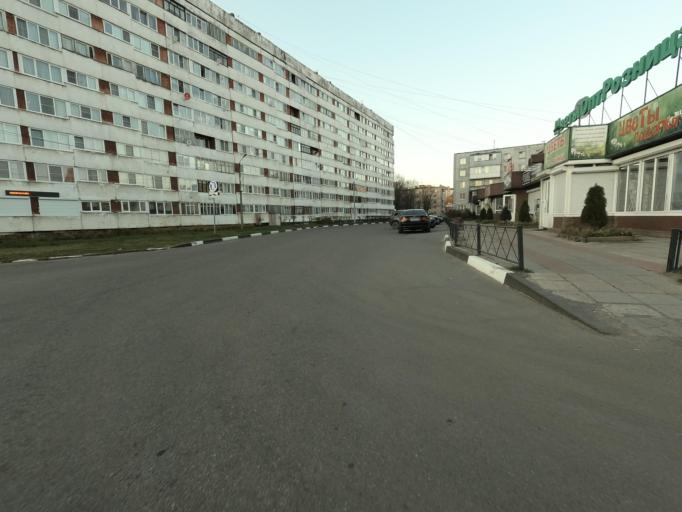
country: RU
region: Leningrad
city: Kirovsk
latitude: 59.8797
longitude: 30.9904
